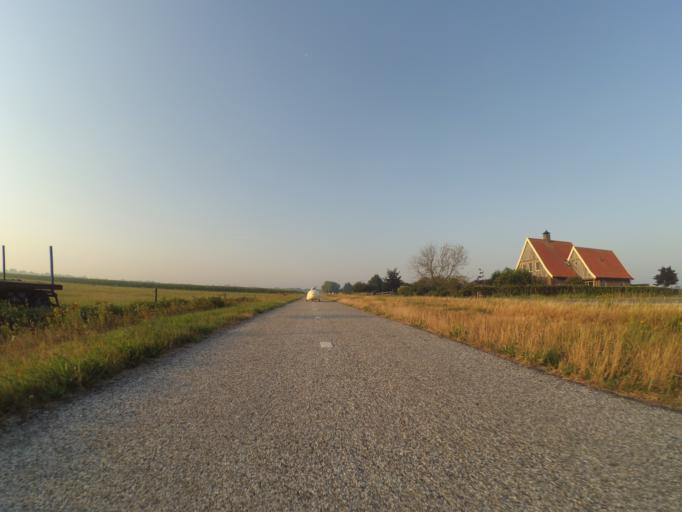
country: NL
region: Overijssel
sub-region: Gemeente Twenterand
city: Vriezenveen
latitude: 52.4280
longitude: 6.6253
